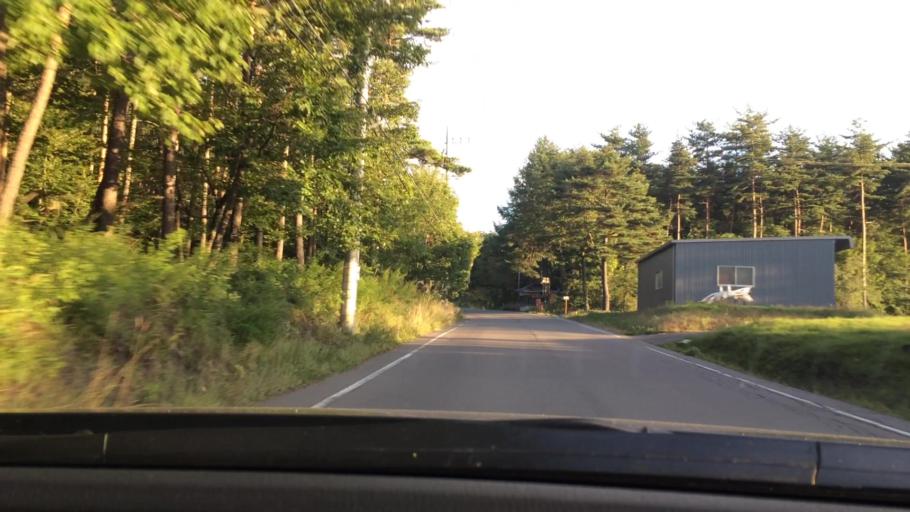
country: JP
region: Nagano
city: Komoro
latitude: 36.4905
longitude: 138.5122
